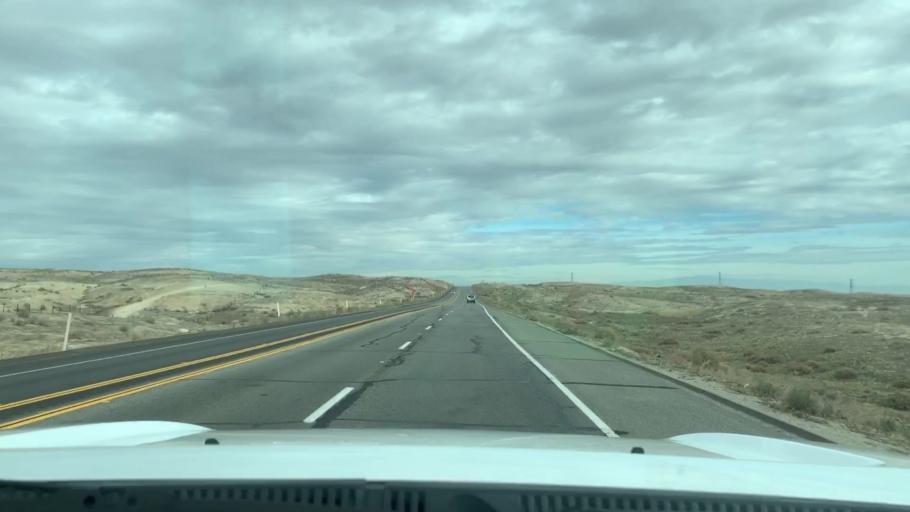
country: US
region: California
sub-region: Kern County
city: Ford City
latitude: 35.2513
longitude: -119.3378
